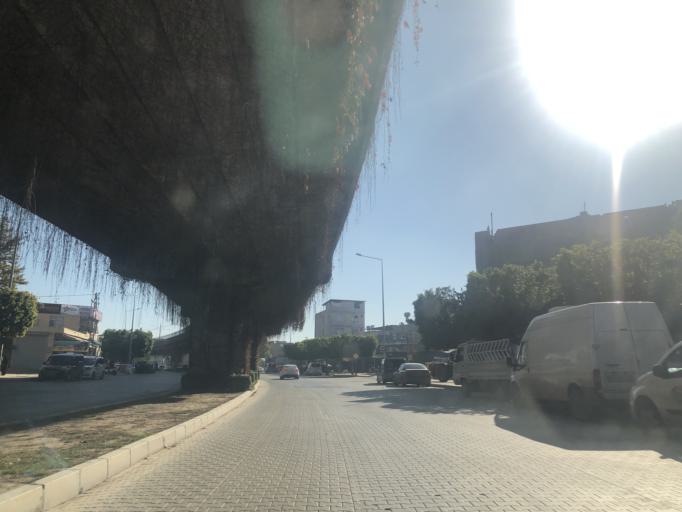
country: TR
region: Adana
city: Seyhan
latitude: 36.9798
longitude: 35.3225
